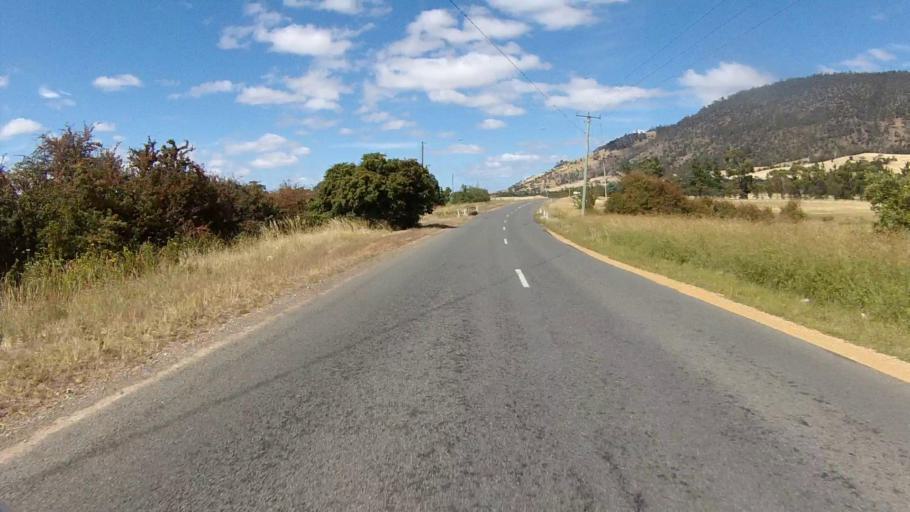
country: AU
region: Tasmania
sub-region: Sorell
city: Sorell
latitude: -42.6214
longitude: 147.4297
